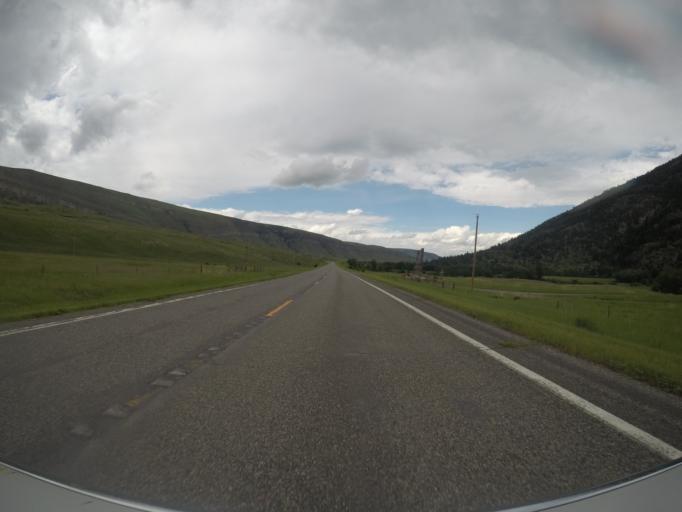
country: US
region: Montana
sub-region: Sweet Grass County
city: Big Timber
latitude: 45.5574
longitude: -110.2030
